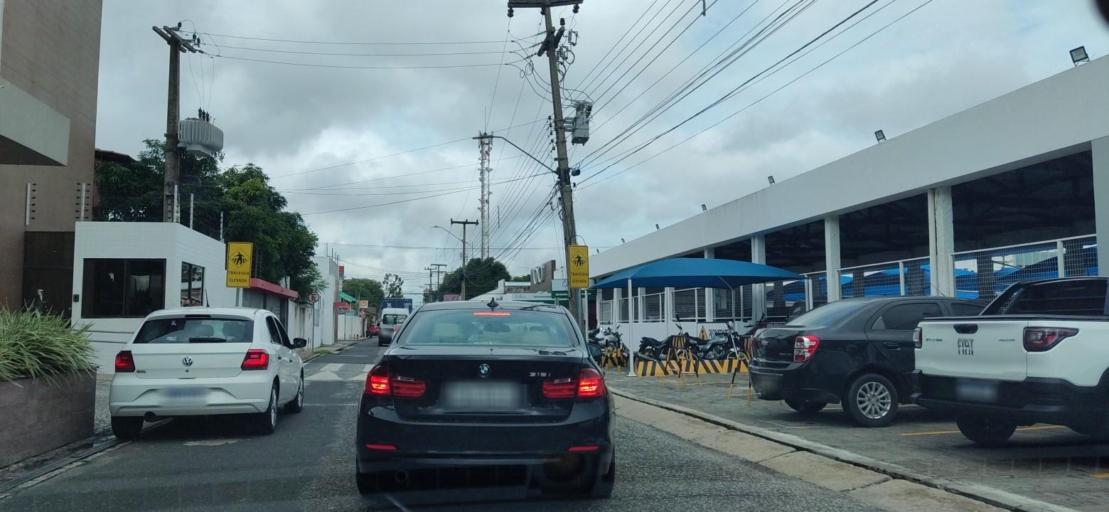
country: BR
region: Piaui
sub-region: Teresina
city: Teresina
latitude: -5.0818
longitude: -42.8079
